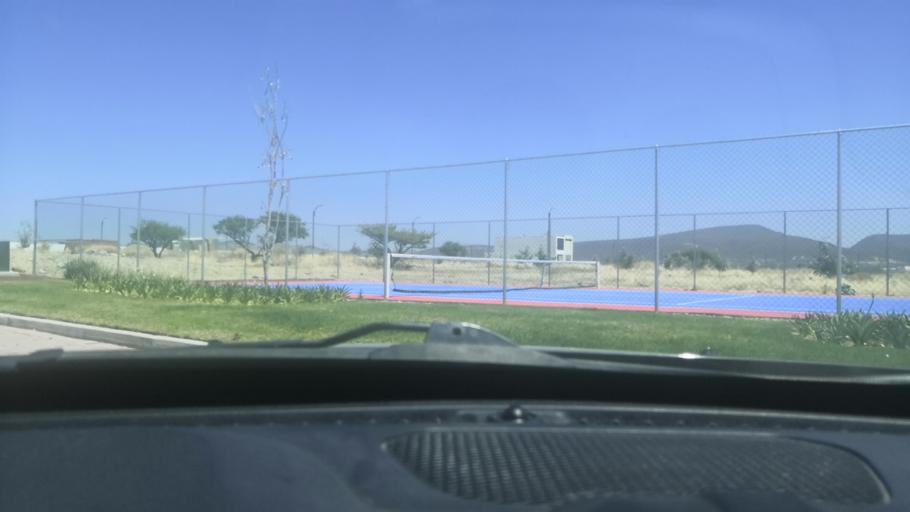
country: MX
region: Guanajuato
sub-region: Leon
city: Fraccionamiento Paseo de las Torres
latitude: 21.2320
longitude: -101.8124
